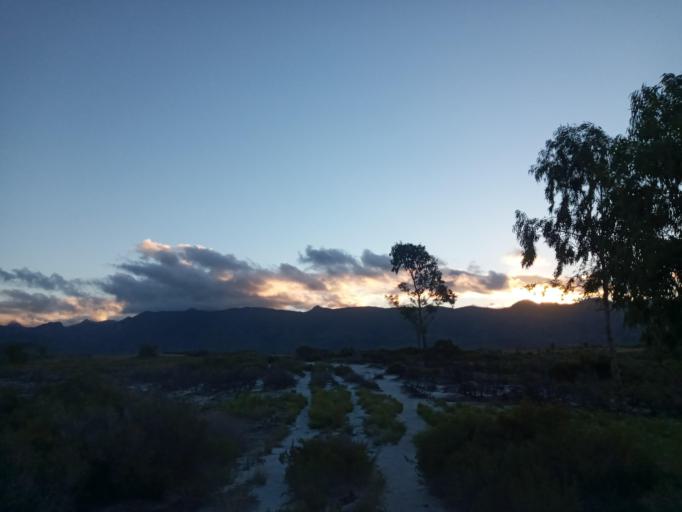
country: MG
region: Anosy
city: Fort Dauphin
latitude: -24.5137
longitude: 47.2328
